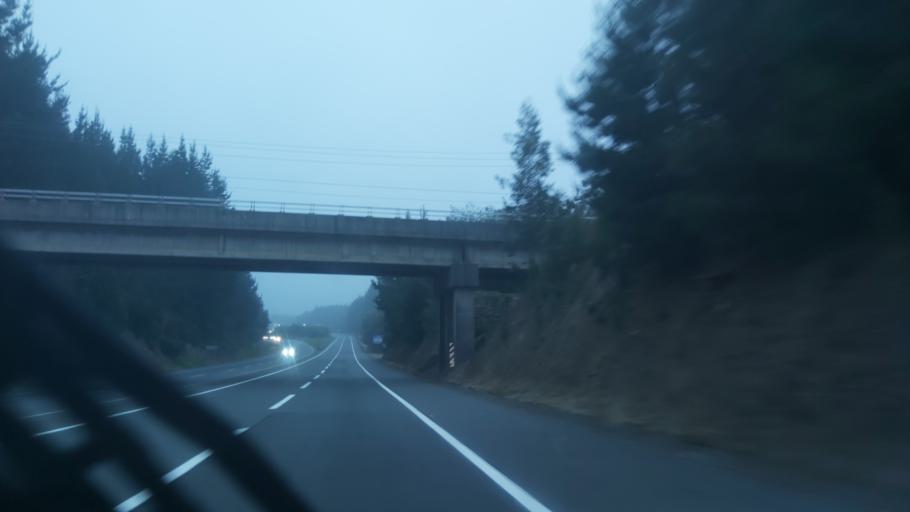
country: CL
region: Biobio
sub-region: Provincia de Concepcion
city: Penco
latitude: -36.7433
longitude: -72.9127
